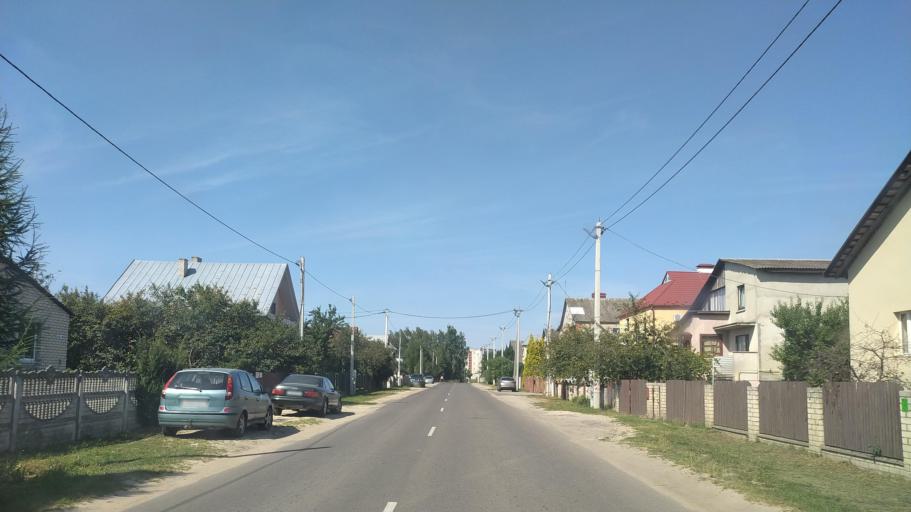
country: BY
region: Brest
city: Byaroza
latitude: 52.5327
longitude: 24.9954
